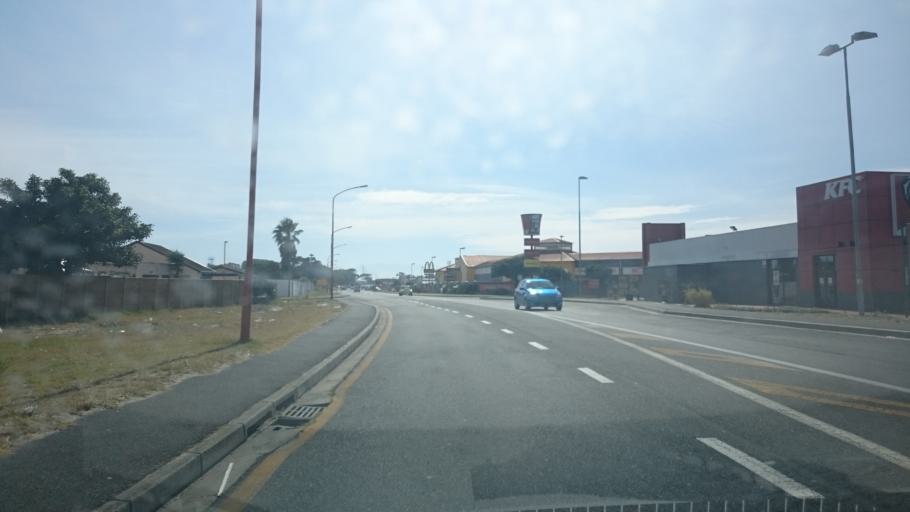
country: ZA
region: Western Cape
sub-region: City of Cape Town
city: Lansdowne
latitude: -34.0178
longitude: 18.5132
